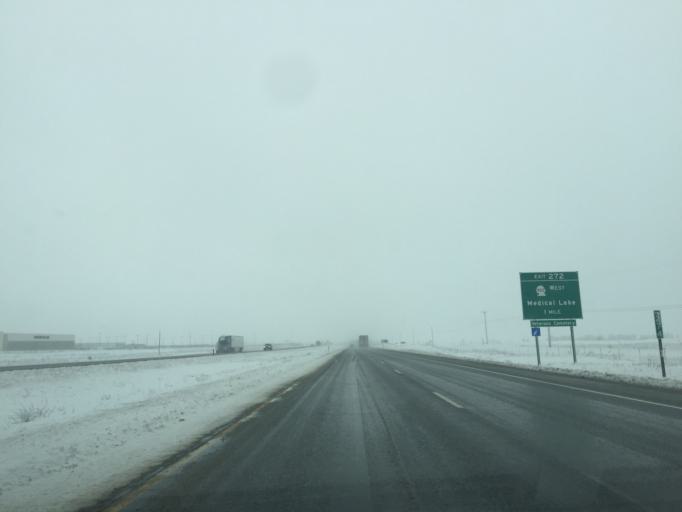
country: US
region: Washington
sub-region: Spokane County
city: Airway Heights
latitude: 47.6017
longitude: -117.5440
